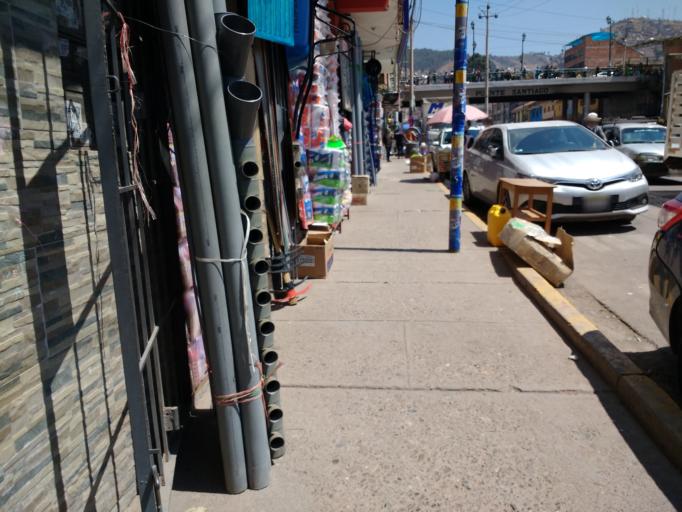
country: PE
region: Cusco
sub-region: Provincia de Cusco
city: Cusco
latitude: -13.5237
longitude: -71.9823
